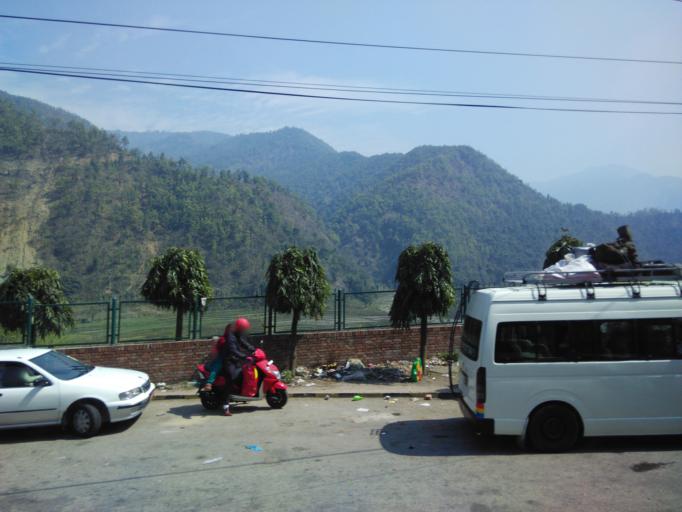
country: NP
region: Central Region
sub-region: Narayani Zone
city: Bharatpur
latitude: 27.8770
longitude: 84.5923
